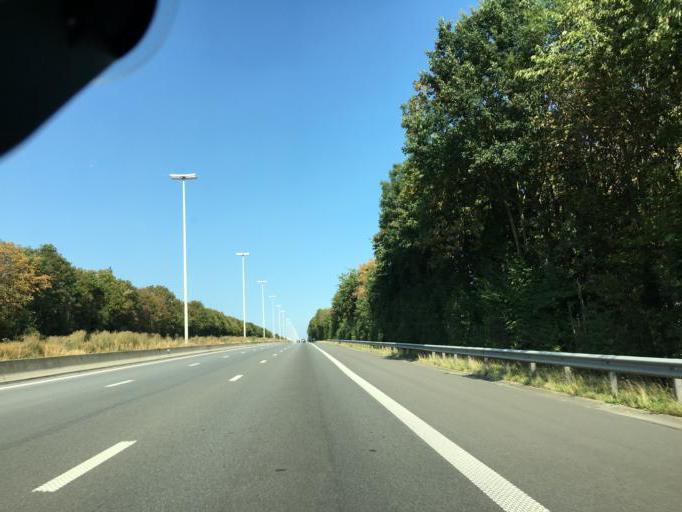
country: BE
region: Wallonia
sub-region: Province de Liege
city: Heron
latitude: 50.5515
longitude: 5.1450
